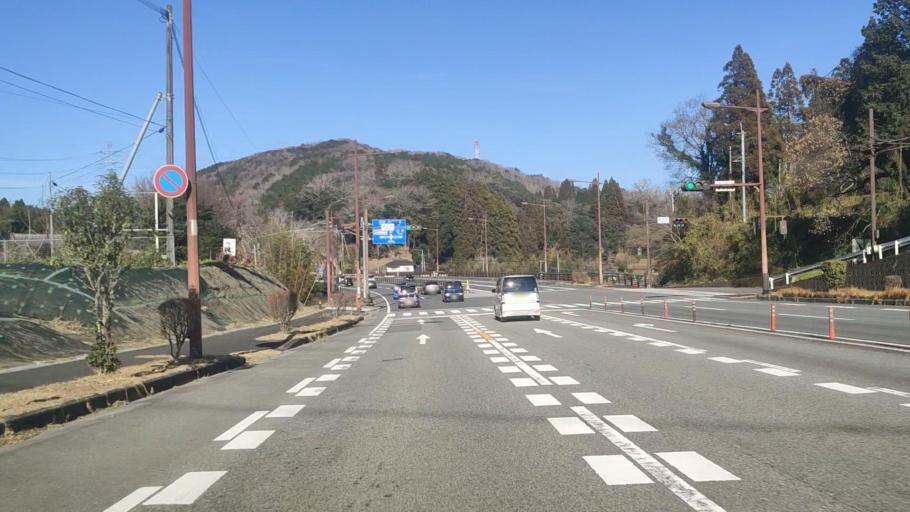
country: JP
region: Oita
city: Oita
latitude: 33.1084
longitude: 131.6560
